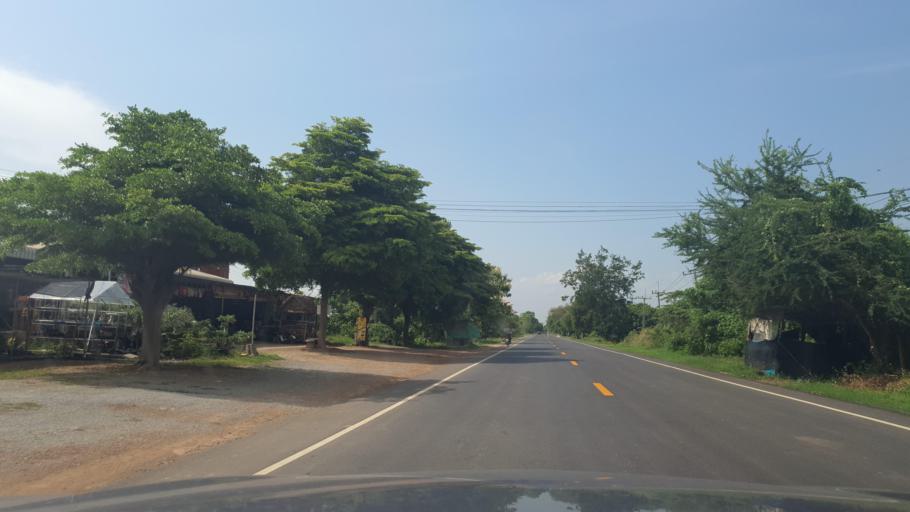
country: TH
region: Sukhothai
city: Si Samrong
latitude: 17.1519
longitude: 99.8257
